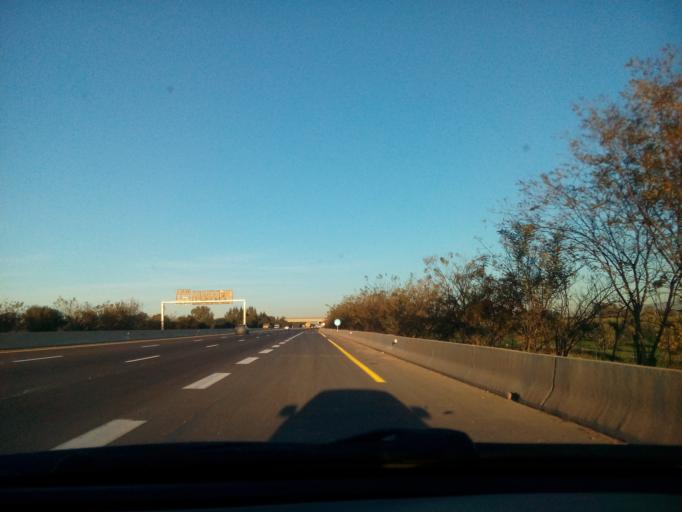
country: DZ
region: Relizane
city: Oued Rhiou
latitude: 35.9696
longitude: 0.9012
